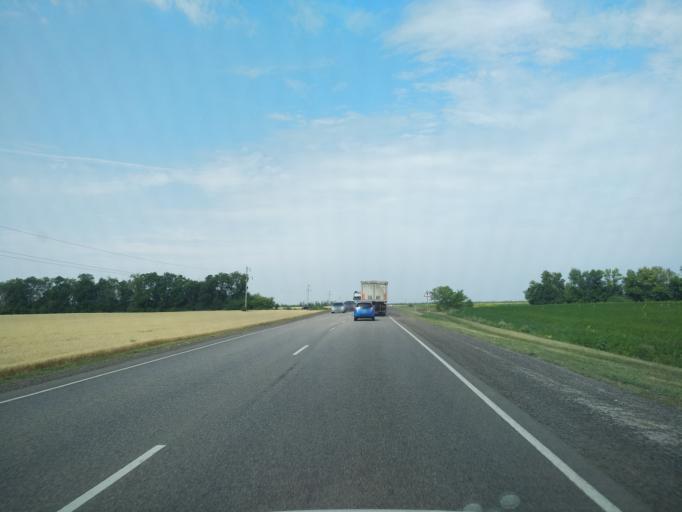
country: RU
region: Voronezj
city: Orlovo
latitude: 51.6835
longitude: 39.5571
